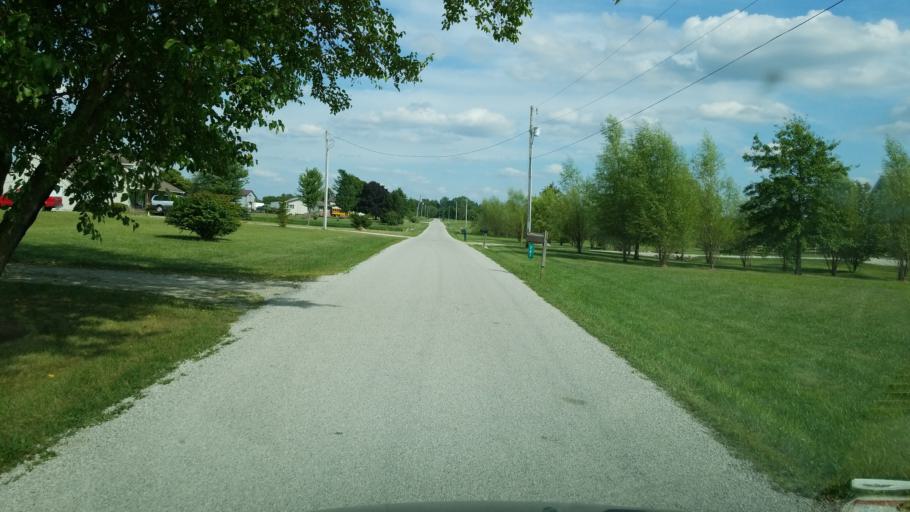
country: US
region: Ohio
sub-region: Delaware County
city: Ashley
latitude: 40.4362
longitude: -83.0085
